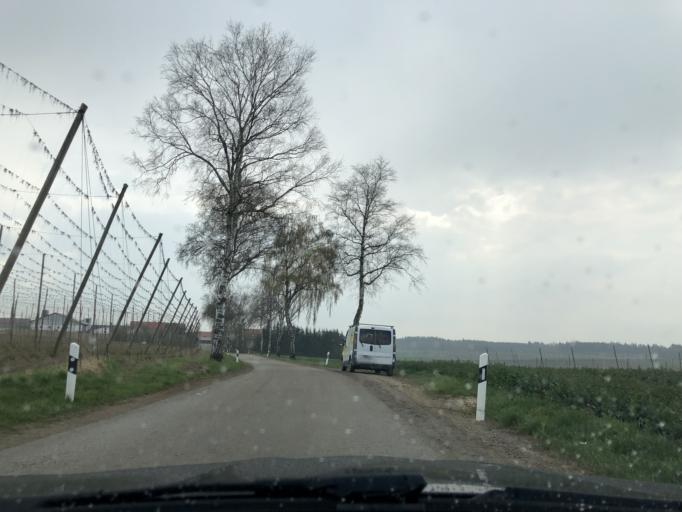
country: DE
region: Bavaria
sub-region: Upper Bavaria
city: Wolfersdorf
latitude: 48.5095
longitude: 11.6768
